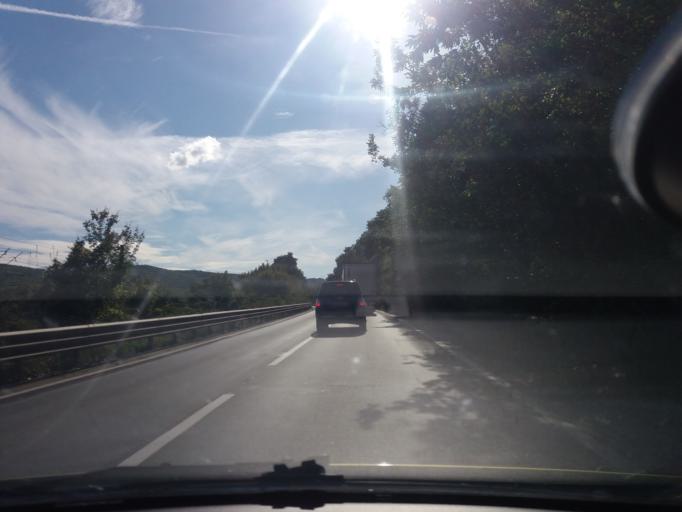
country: RO
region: Arad
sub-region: Comuna Savarsin
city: Savarsin
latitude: 45.9977
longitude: 22.3043
